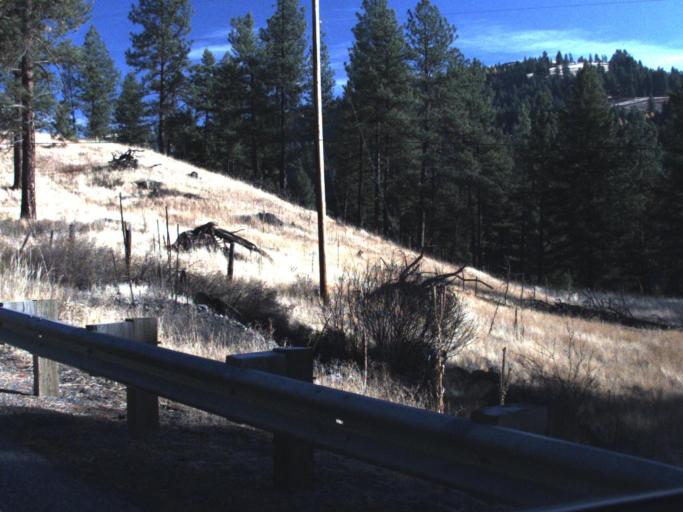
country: US
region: Washington
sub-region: Ferry County
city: Republic
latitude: 48.5818
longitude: -118.7421
